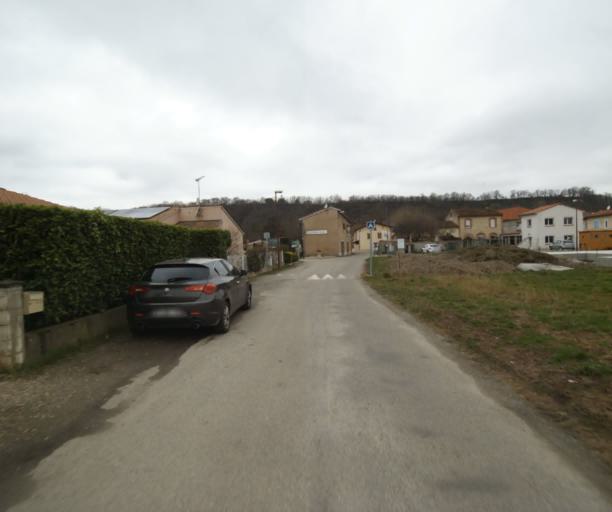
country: FR
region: Midi-Pyrenees
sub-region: Departement de l'Ariege
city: Saverdun
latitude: 43.1840
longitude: 1.6028
